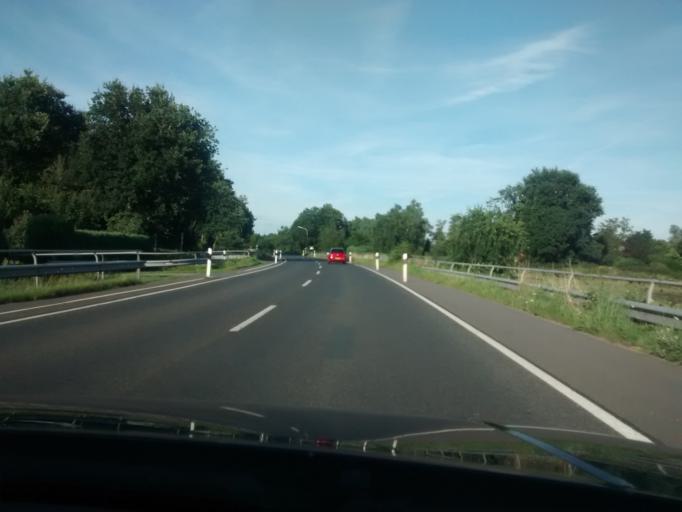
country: DE
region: Lower Saxony
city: Twist
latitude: 52.6468
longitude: 7.1211
